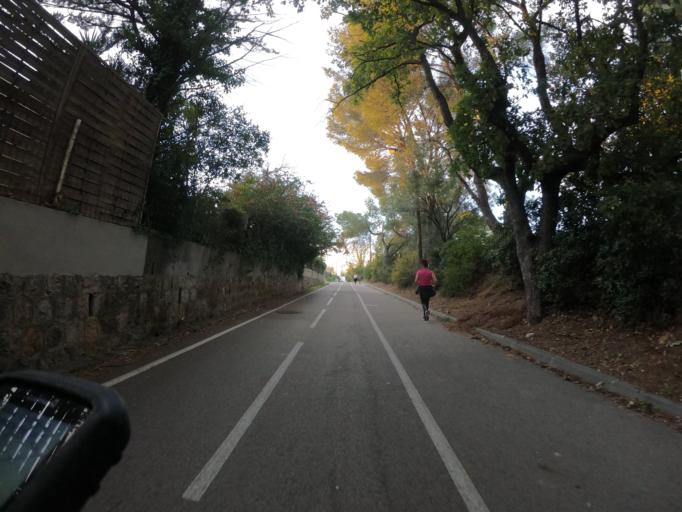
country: FR
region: Provence-Alpes-Cote d'Azur
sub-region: Departement du Var
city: La Garde
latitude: 43.1099
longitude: 5.9985
